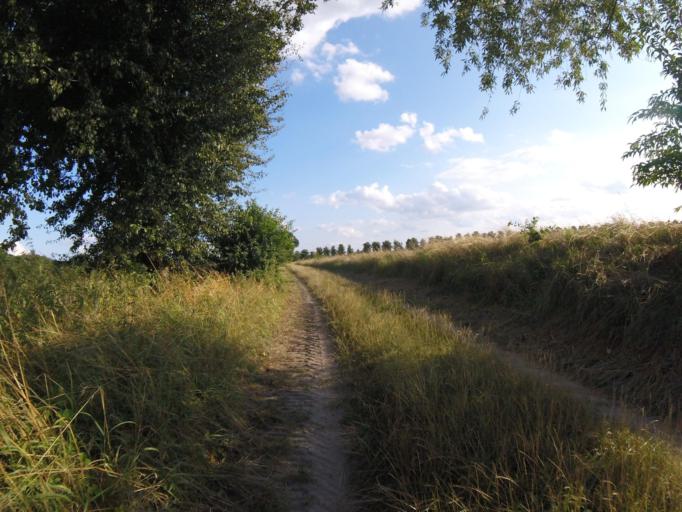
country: DE
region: Brandenburg
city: Mittenwalde
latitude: 52.2950
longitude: 13.5455
